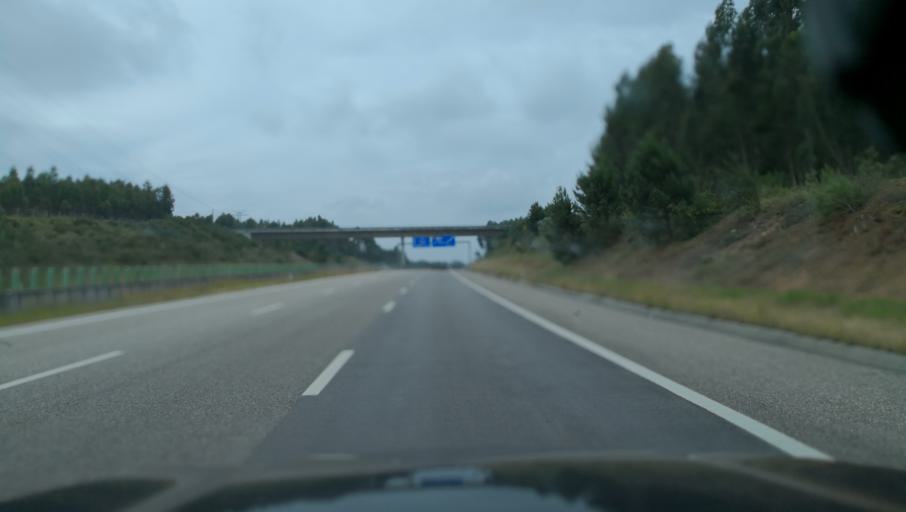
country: PT
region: Coimbra
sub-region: Figueira da Foz
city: Lavos
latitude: 40.0588
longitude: -8.8003
